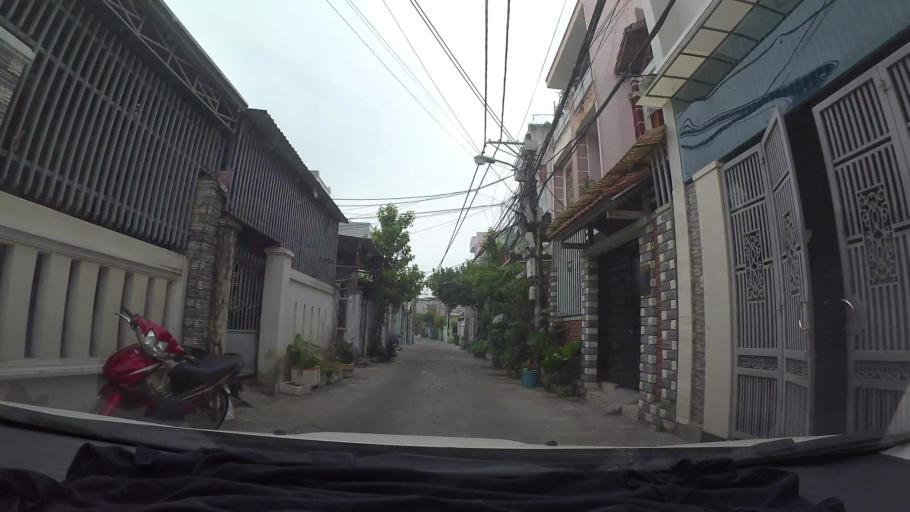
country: VN
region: Da Nang
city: Da Nang
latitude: 16.0456
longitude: 108.2066
